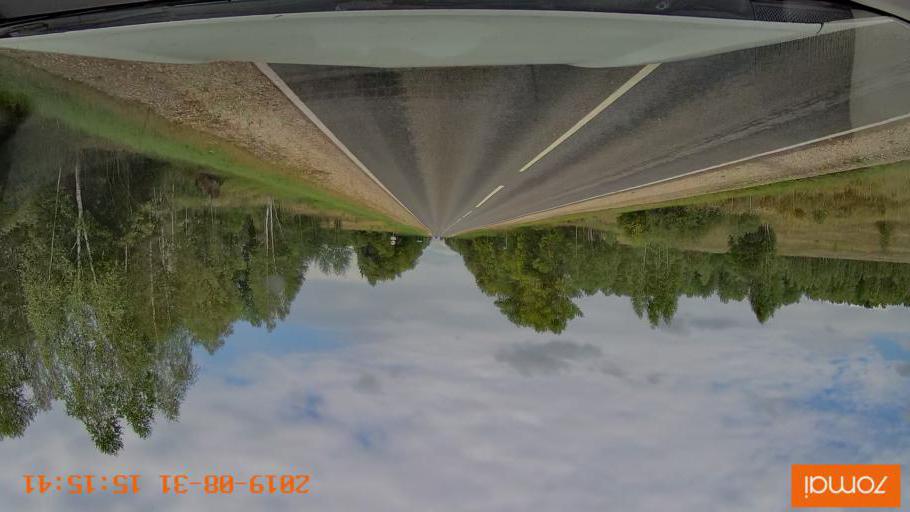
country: RU
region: Kaluga
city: Baryatino
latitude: 54.4536
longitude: 34.3323
